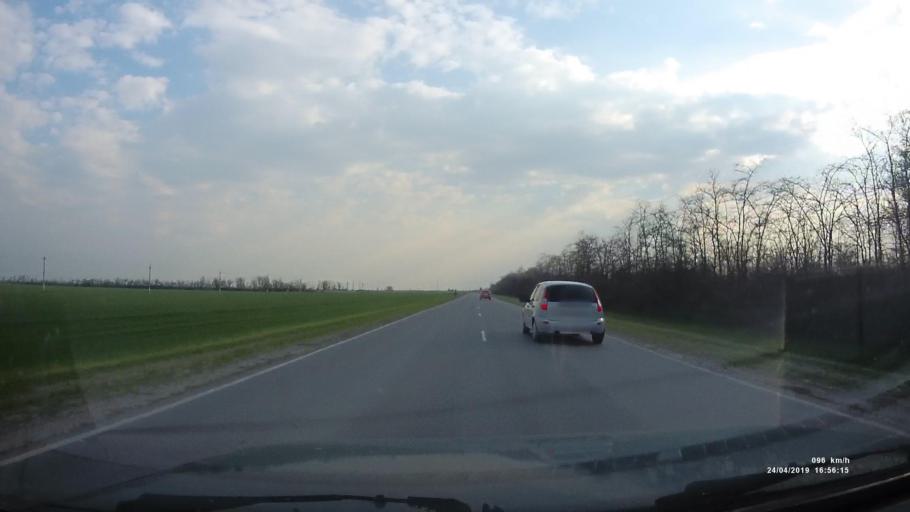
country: RU
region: Rostov
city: Proletarsk
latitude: 46.6542
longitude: 41.6802
